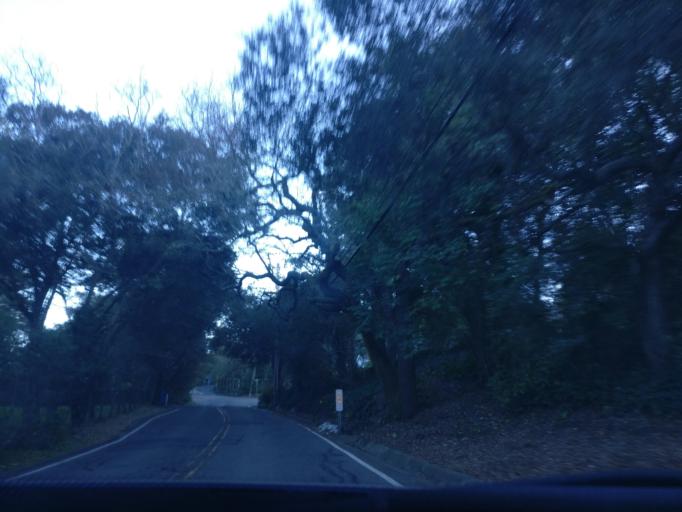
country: US
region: California
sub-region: Contra Costa County
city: Orinda
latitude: 37.8861
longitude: -122.1958
